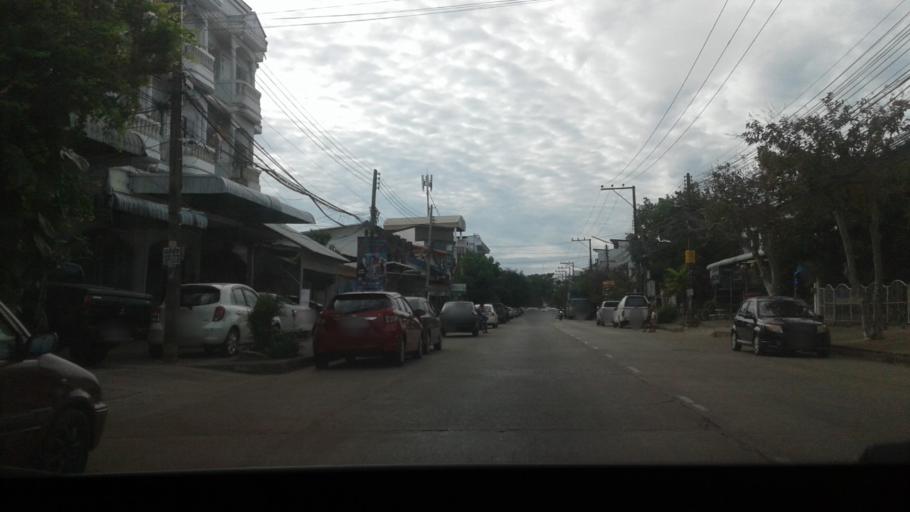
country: TH
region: Changwat Udon Thani
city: Udon Thani
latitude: 17.4167
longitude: 102.7950
